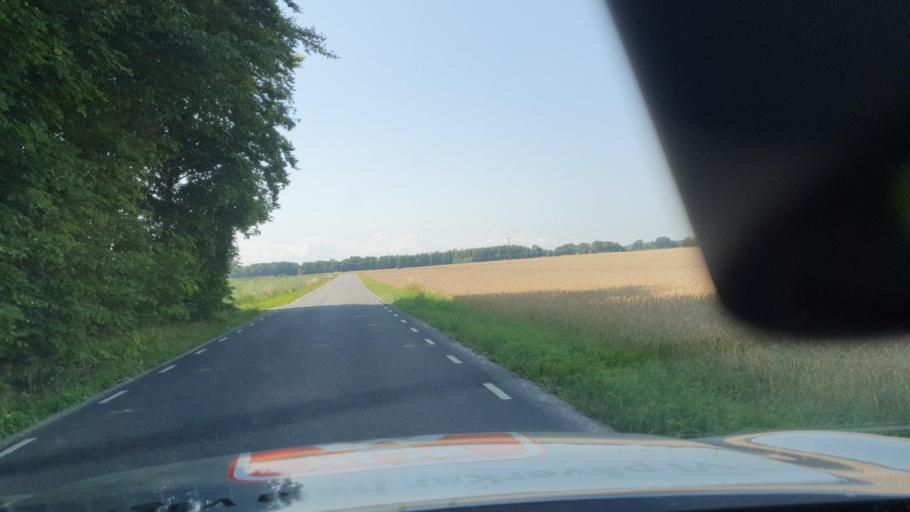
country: SE
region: Skane
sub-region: Bromolla Kommun
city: Bromoella
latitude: 56.0470
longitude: 14.4027
